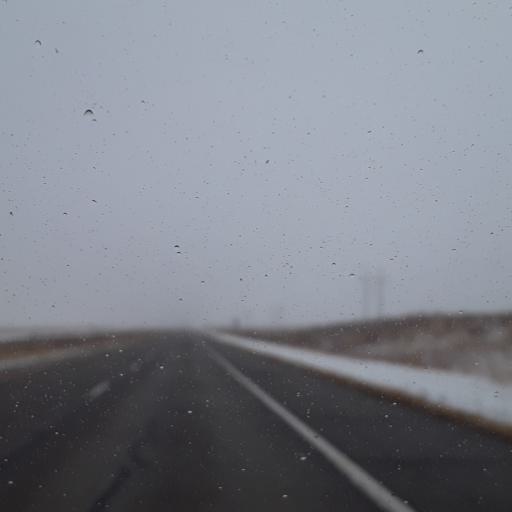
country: US
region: Colorado
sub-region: Logan County
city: Sterling
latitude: 40.7720
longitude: -102.9347
